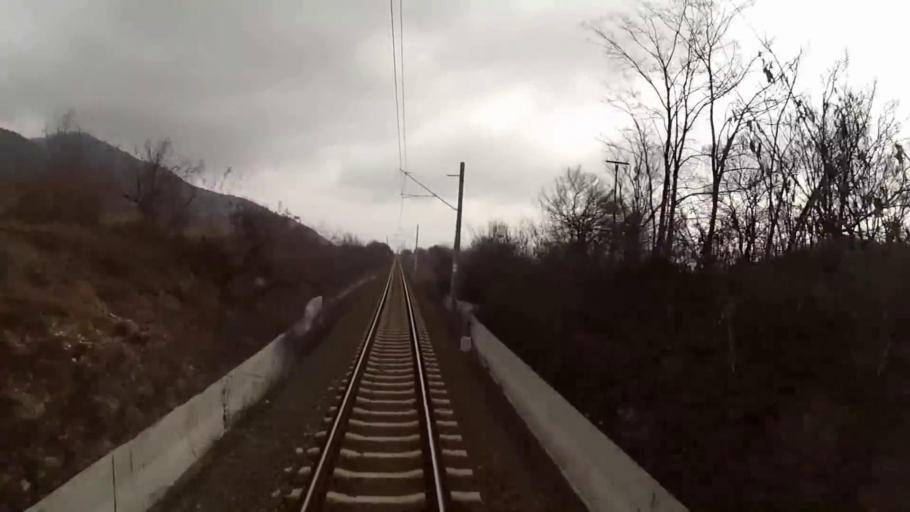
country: BG
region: Sofiya
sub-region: Obshtina Chavdar
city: Chavdar
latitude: 42.6919
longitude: 24.0382
